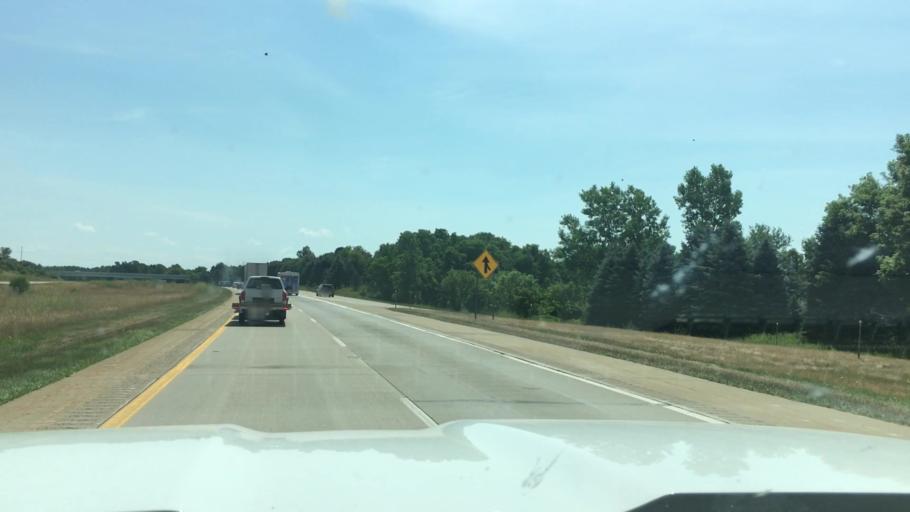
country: US
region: Michigan
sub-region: Ingham County
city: Haslett
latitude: 42.7814
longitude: -84.4059
